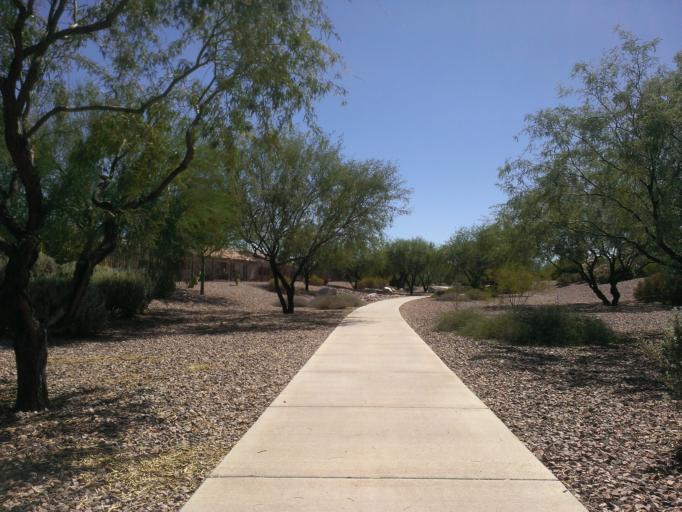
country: US
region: Arizona
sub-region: Pinal County
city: Arizona City
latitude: 32.8125
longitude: -111.6370
